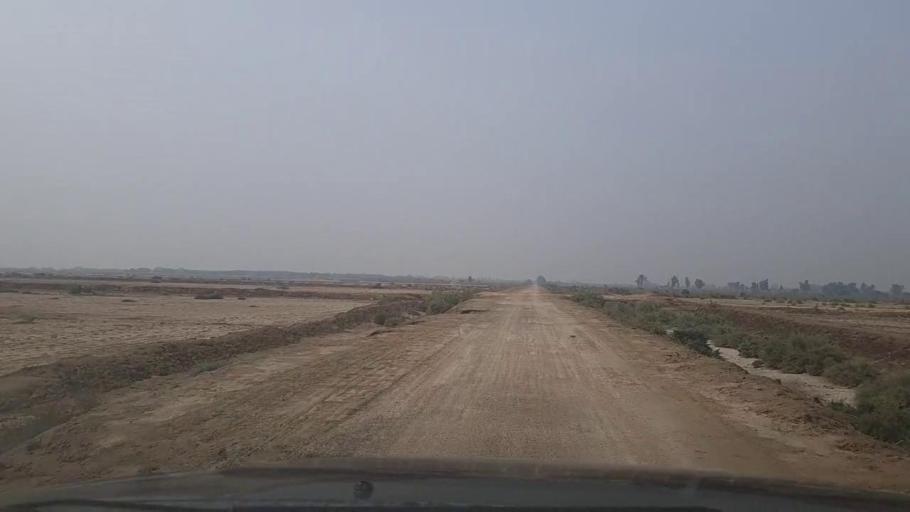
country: PK
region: Sindh
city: Mirpur Sakro
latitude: 24.5373
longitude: 67.7823
